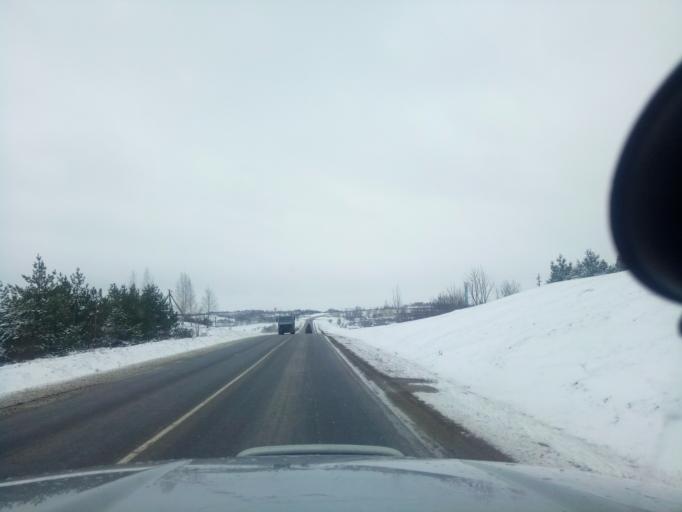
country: BY
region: Minsk
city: Kapyl'
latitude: 53.1413
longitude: 27.0831
